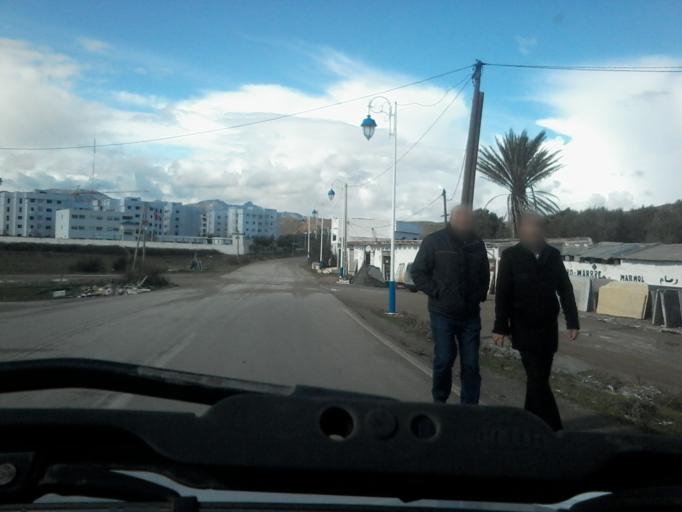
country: MA
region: Tanger-Tetouan
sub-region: Tetouan
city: Martil
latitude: 35.7028
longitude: -5.3561
